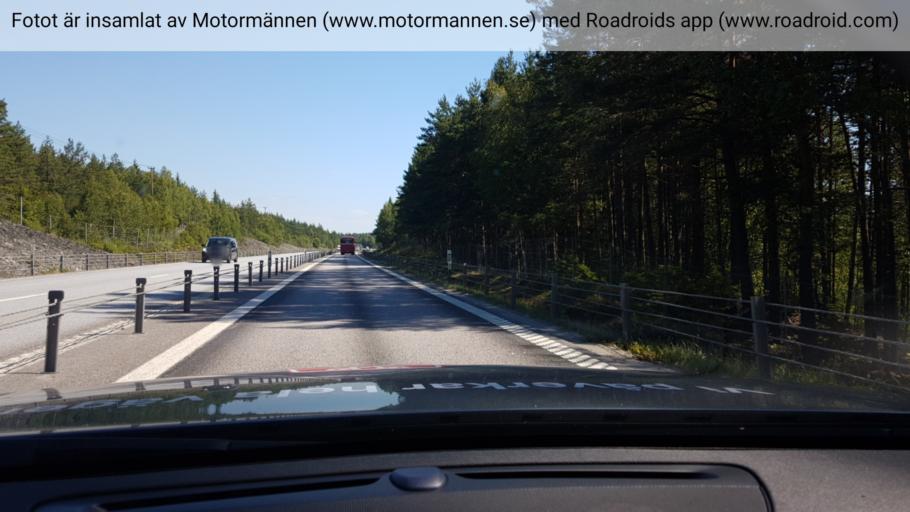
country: SE
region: Stockholm
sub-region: Osterakers Kommun
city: Akersberga
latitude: 59.5853
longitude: 18.2533
